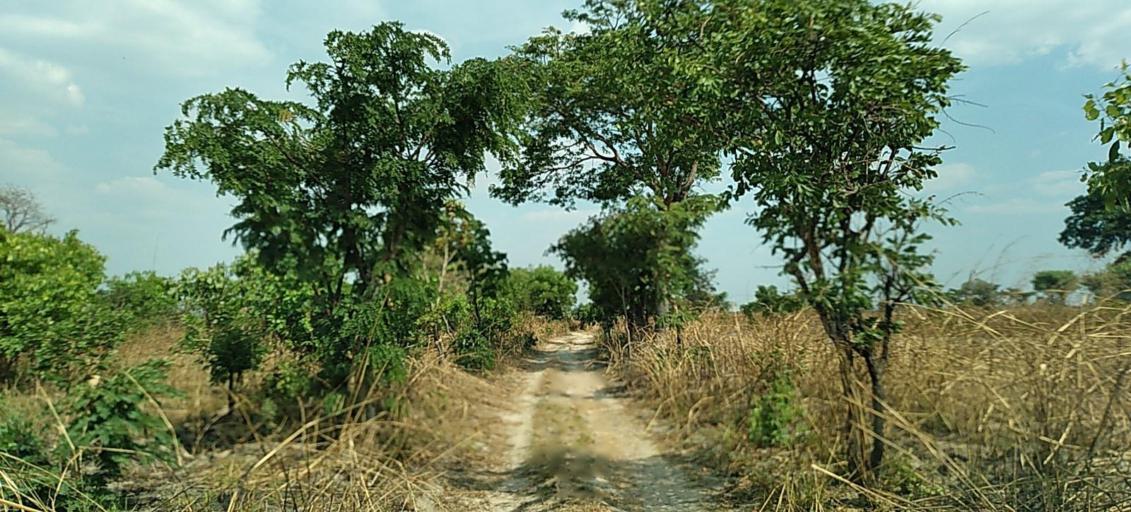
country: ZM
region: Copperbelt
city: Chililabombwe
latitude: -12.3426
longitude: 27.7866
